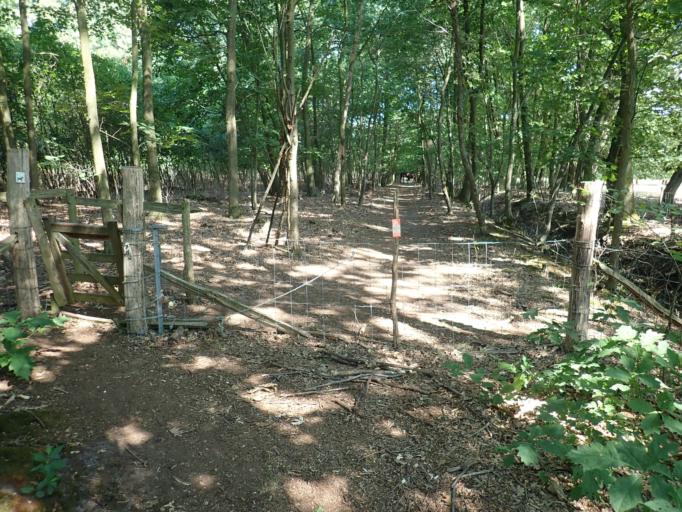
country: BE
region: Flanders
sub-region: Provincie Vlaams-Brabant
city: Scherpenheuvel-Zichem
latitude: 51.0158
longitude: 5.0080
